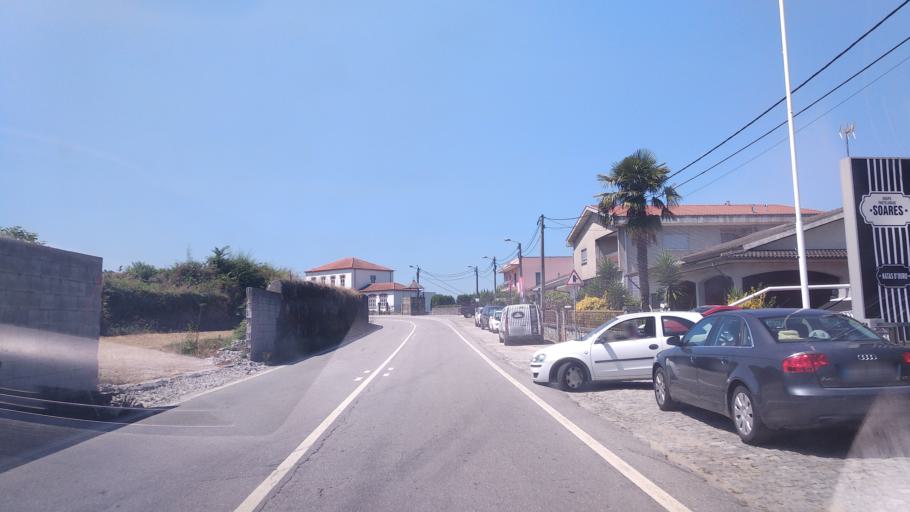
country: PT
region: Braga
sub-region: Braga
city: Adaufe
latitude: 41.5858
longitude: -8.4032
